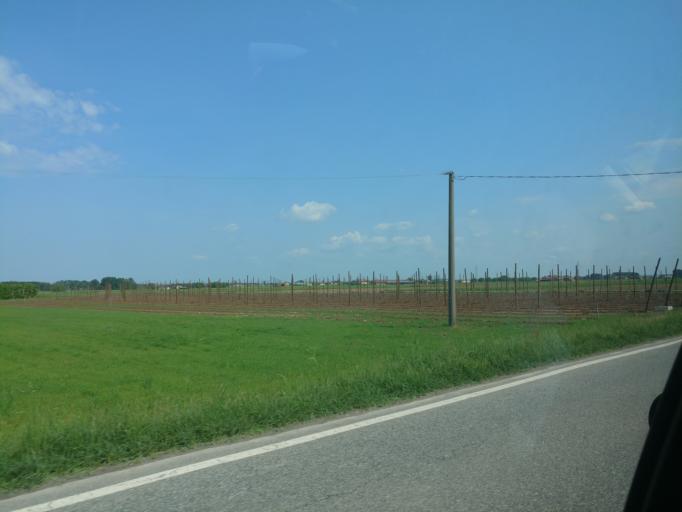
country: IT
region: Piedmont
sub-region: Provincia di Torino
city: Cavour
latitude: 44.7605
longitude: 7.3991
